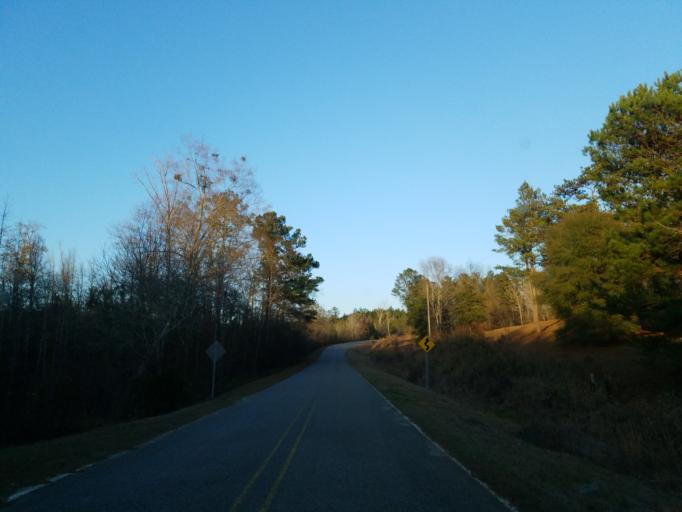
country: US
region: Mississippi
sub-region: Lauderdale County
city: Meridian
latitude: 32.2664
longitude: -88.7796
